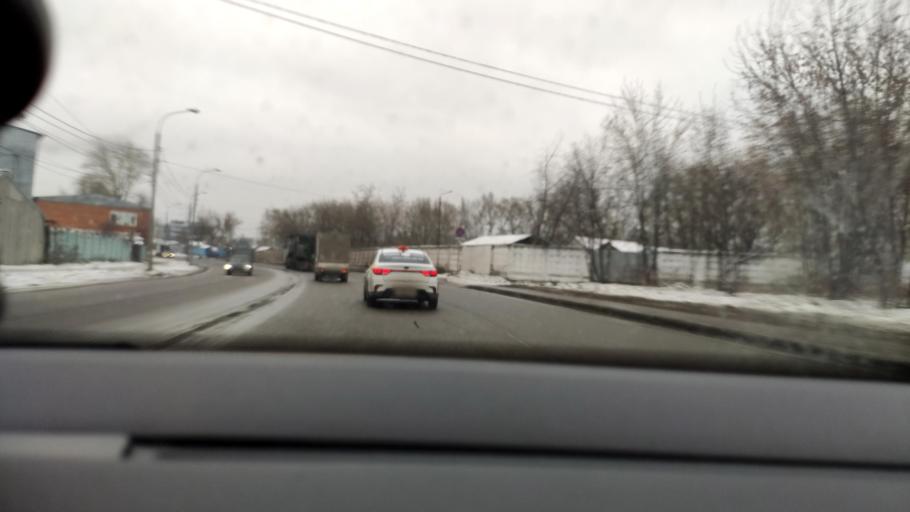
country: RU
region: Moscow
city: Khimki
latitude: 55.9090
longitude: 37.4199
